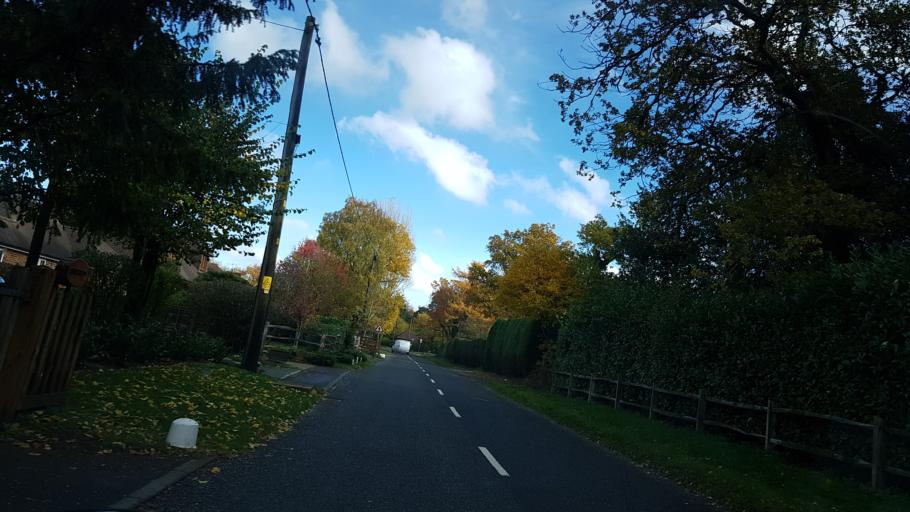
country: GB
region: England
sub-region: Surrey
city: Seale
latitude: 51.2217
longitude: -0.7356
